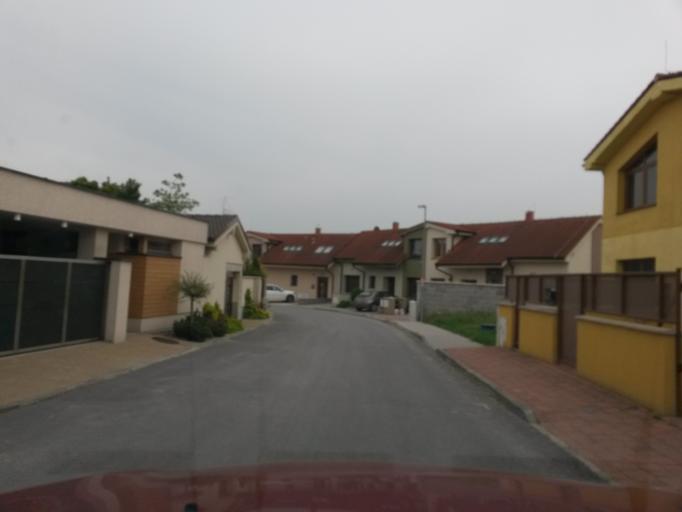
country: SK
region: Kosicky
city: Kosice
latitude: 48.7021
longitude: 21.2233
